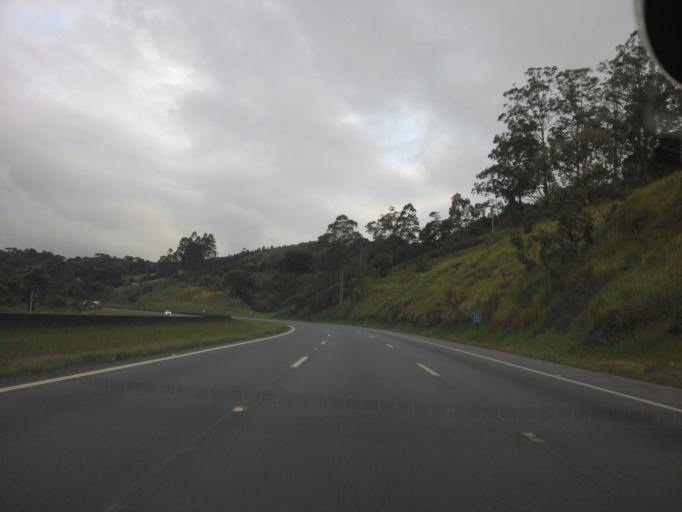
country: BR
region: Sao Paulo
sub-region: Piracaia
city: Piracaia
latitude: -23.1808
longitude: -46.3110
